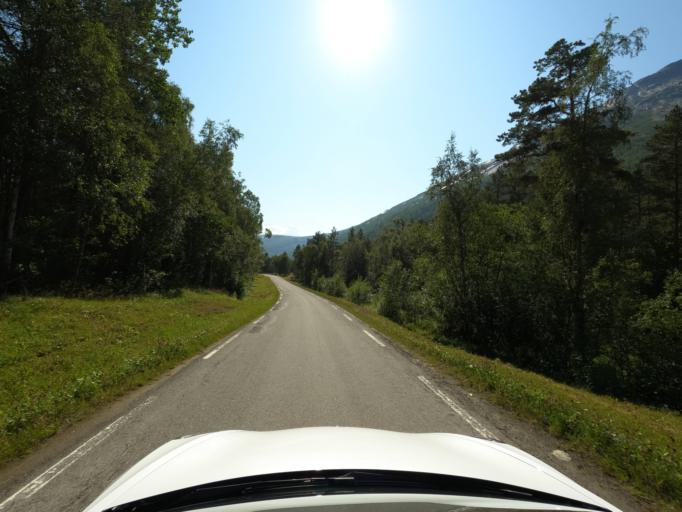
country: NO
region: Nordland
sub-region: Narvik
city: Narvik
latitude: 68.1903
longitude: 17.5525
